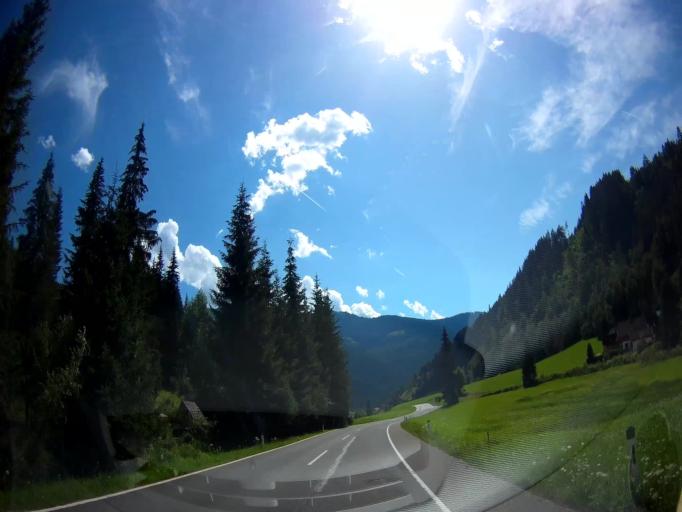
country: AT
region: Salzburg
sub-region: Politischer Bezirk Tamsweg
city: Ramingstein
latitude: 47.0713
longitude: 13.8034
